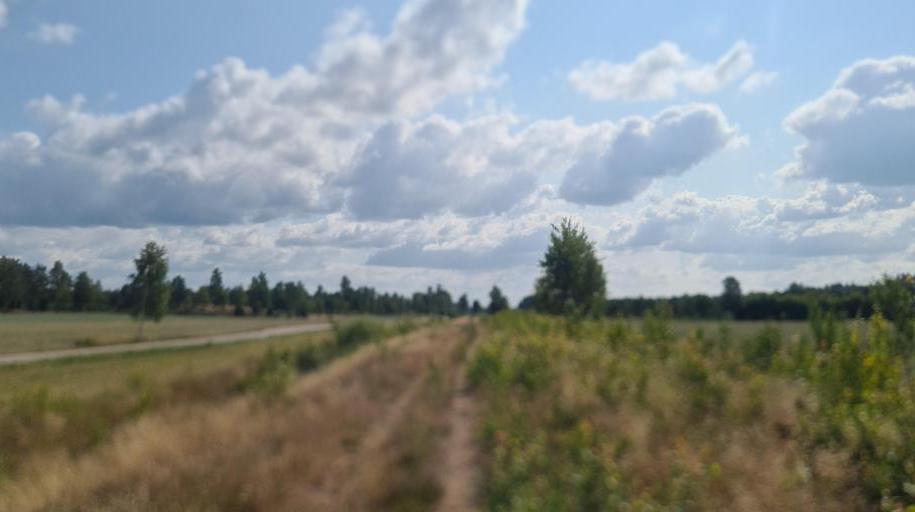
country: SE
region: Kronoberg
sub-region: Ljungby Kommun
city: Ljungby
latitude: 56.7524
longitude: 13.8841
